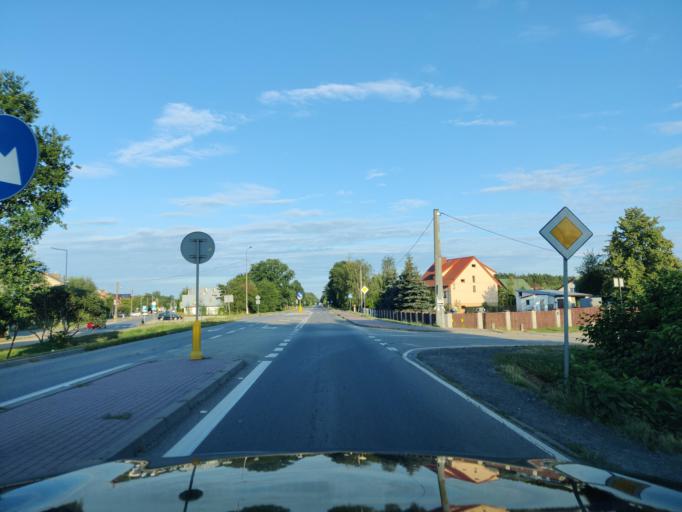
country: PL
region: Masovian Voivodeship
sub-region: Powiat pultuski
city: Pultusk
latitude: 52.6845
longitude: 21.1135
